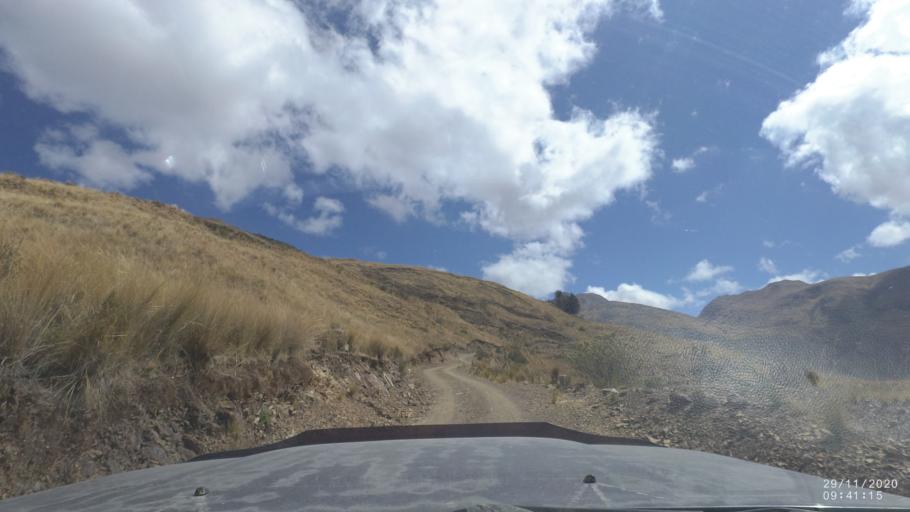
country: BO
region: Cochabamba
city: Cochabamba
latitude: -17.3035
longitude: -66.1827
